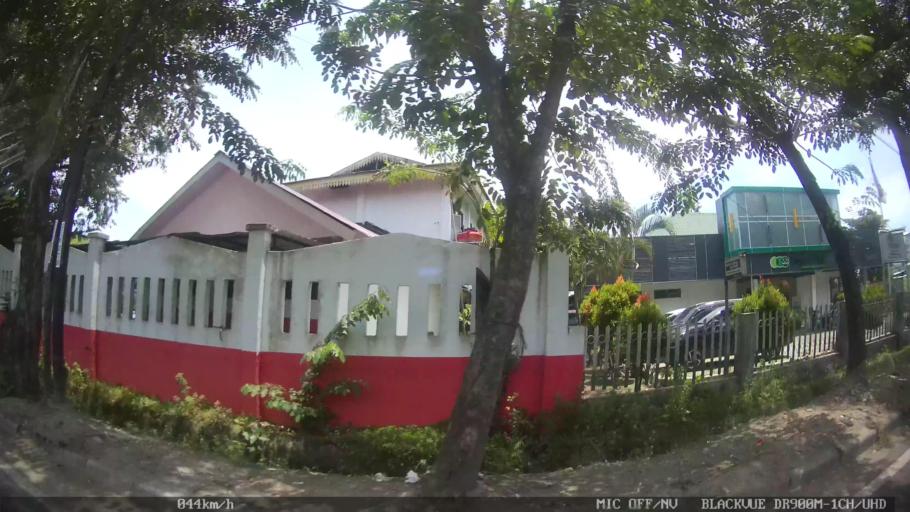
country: ID
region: North Sumatra
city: Labuhan Deli
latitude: 3.7274
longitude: 98.6776
